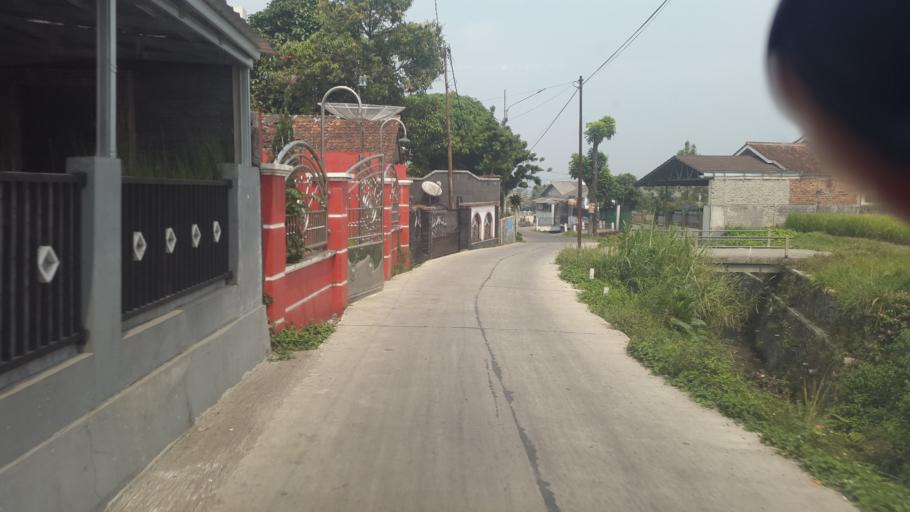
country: ID
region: West Java
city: Sukabumi
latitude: -6.9109
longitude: 106.8895
